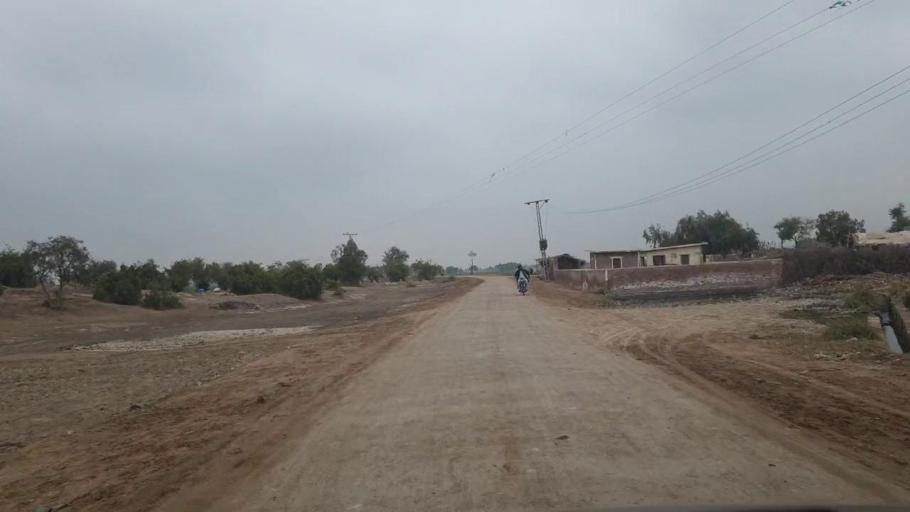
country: PK
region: Sindh
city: Shahdadpur
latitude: 25.9495
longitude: 68.7241
